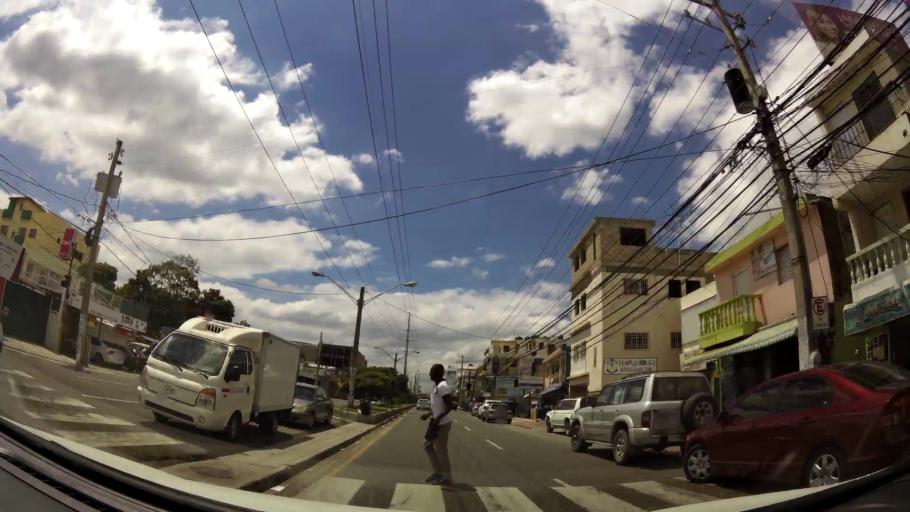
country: DO
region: Nacional
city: Bella Vista
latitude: 18.4350
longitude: -69.9592
